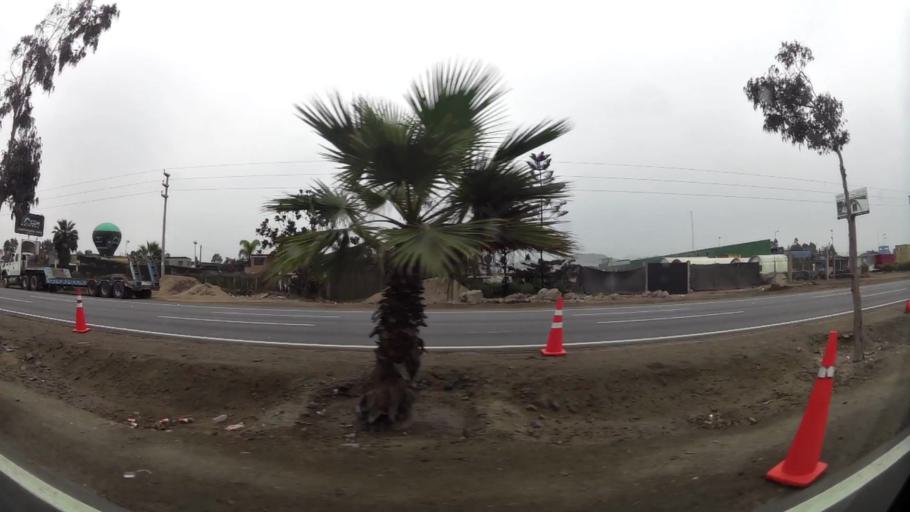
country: PE
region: Lima
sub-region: Lima
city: Punta Hermosa
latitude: -12.2787
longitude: -76.8857
